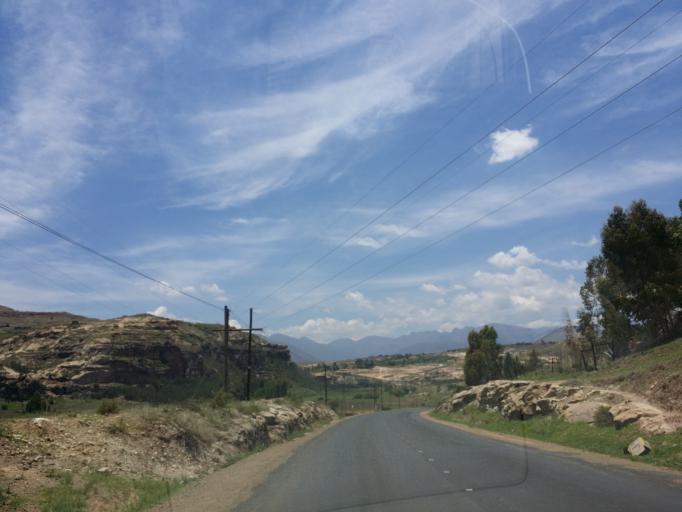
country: LS
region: Butha-Buthe
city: Butha-Buthe
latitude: -28.7337
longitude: 28.4082
